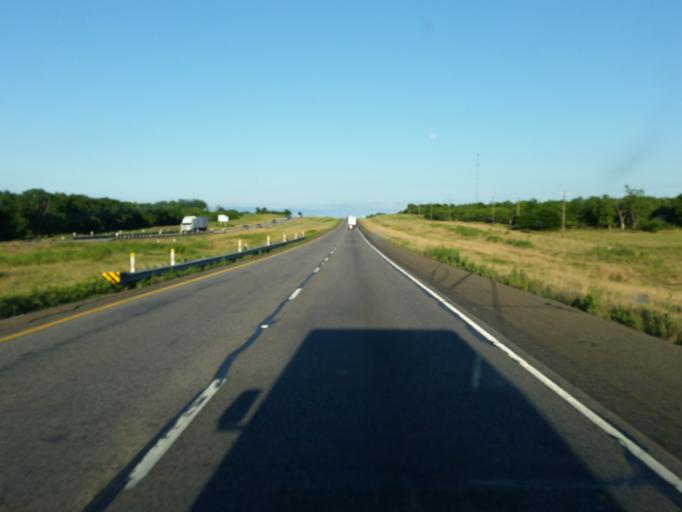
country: US
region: Texas
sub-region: Kaufman County
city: Terrell
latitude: 32.6881
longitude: -96.2239
